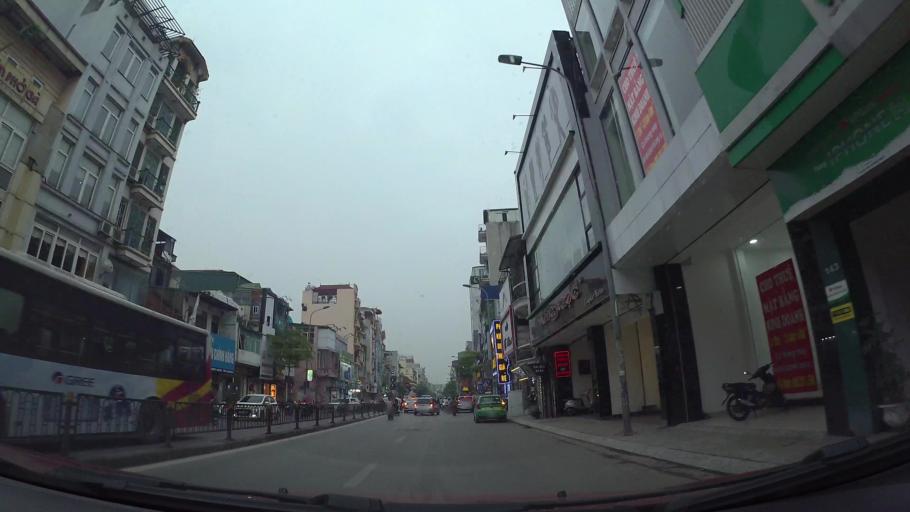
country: VN
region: Ha Noi
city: Dong Da
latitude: 21.0231
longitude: 105.8321
